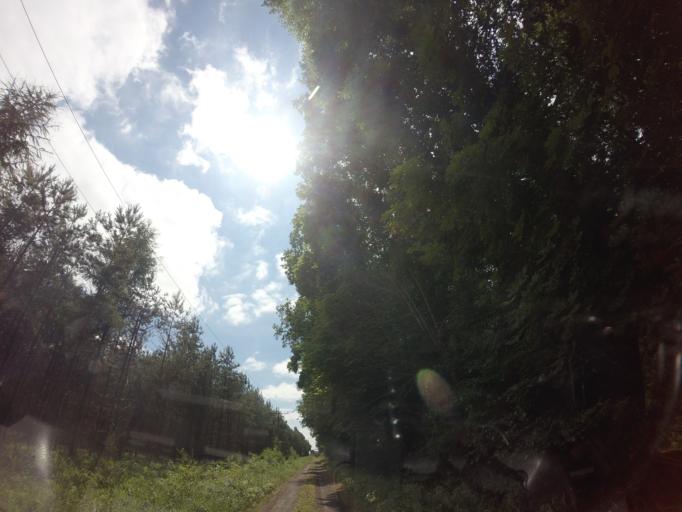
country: PL
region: West Pomeranian Voivodeship
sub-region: Powiat choszczenski
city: Krzecin
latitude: 52.9882
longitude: 15.4823
